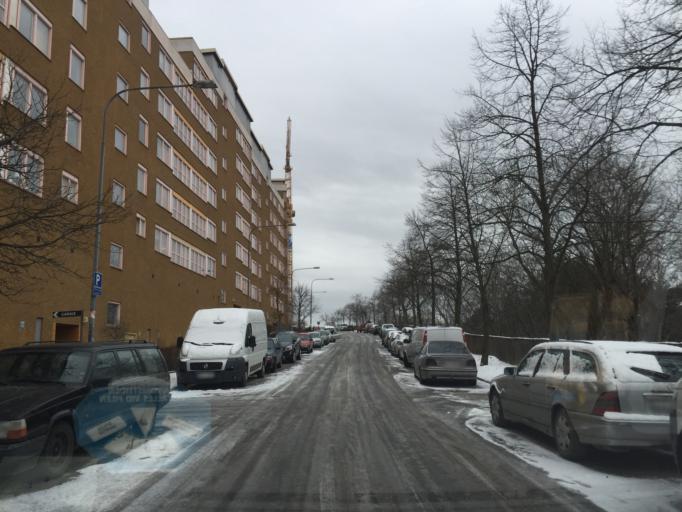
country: SE
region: Stockholm
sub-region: Stockholms Kommun
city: OEstermalm
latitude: 59.3117
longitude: 18.1136
